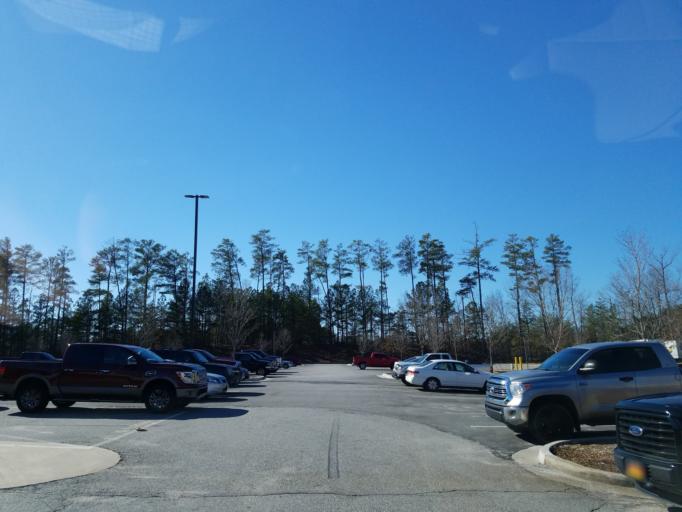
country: US
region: Georgia
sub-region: Fulton County
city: Alpharetta
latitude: 34.0510
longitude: -84.3223
